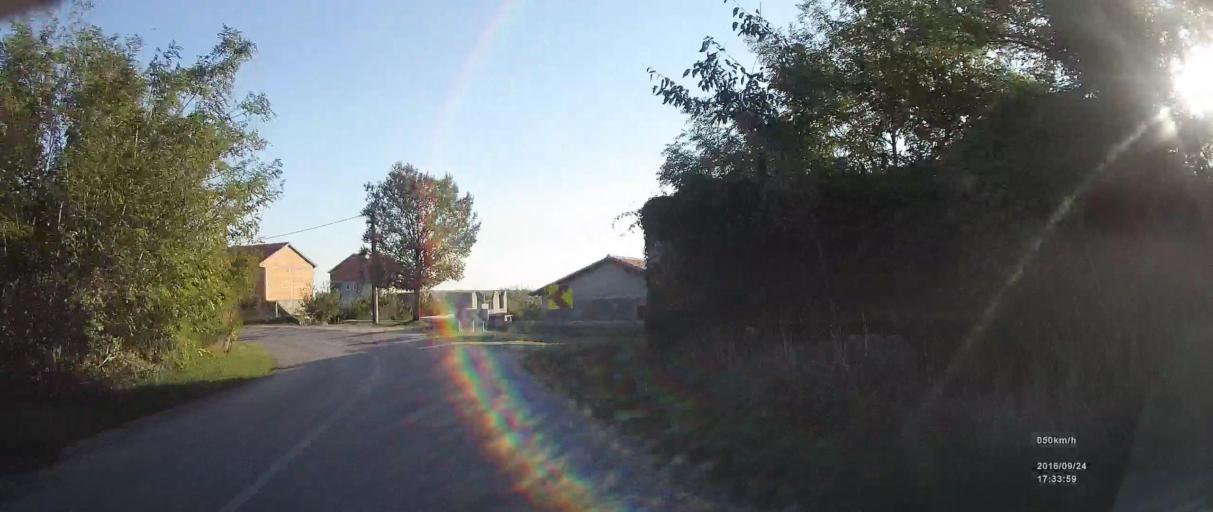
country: HR
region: Zadarska
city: Posedarje
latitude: 44.1698
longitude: 15.4569
